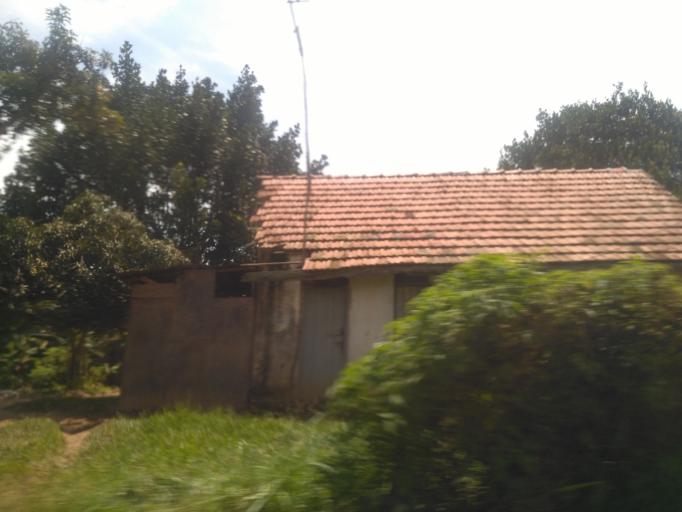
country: UG
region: Central Region
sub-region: Wakiso District
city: Entebbe
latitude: 0.0691
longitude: 32.4787
